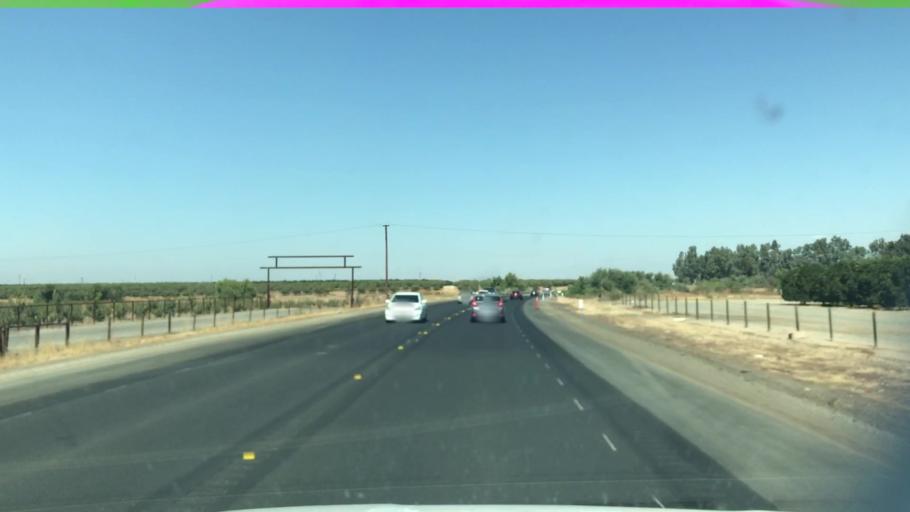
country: US
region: California
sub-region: Tulare County
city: Terra Bella
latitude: 35.9775
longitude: -119.0536
